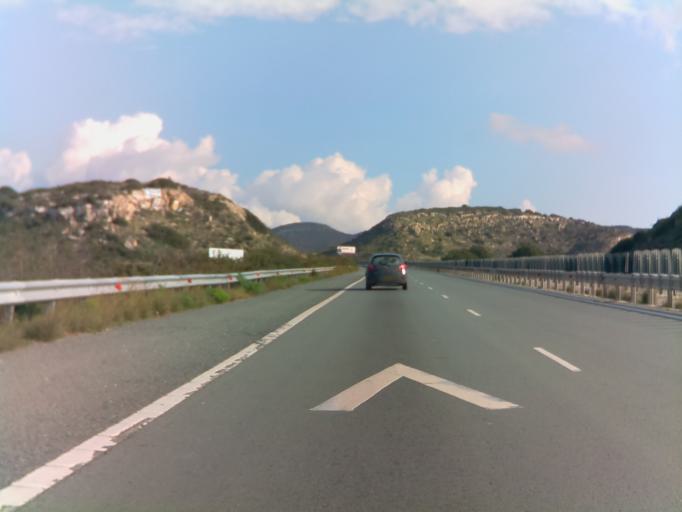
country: CY
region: Larnaka
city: Kofinou
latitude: 34.7670
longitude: 33.3327
